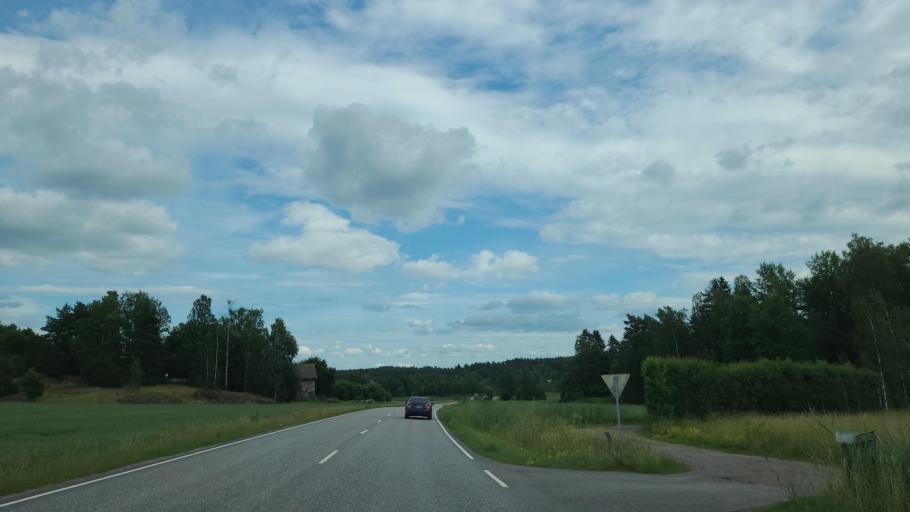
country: FI
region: Varsinais-Suomi
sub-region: Turku
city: Rymaettylae
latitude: 60.3821
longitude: 21.9378
